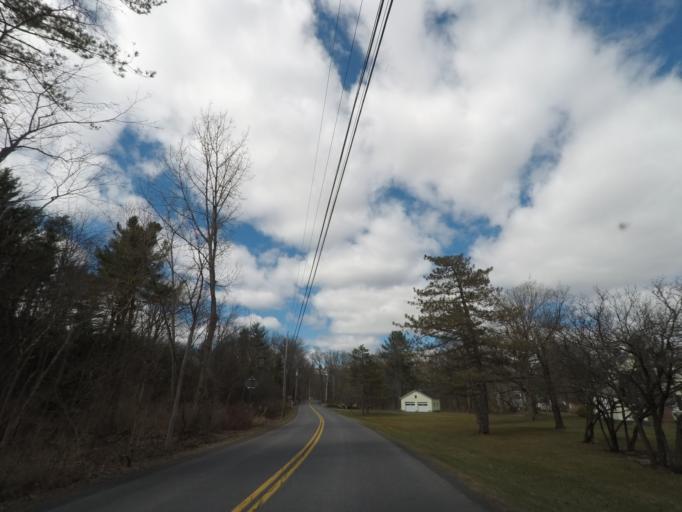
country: US
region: New York
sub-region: Albany County
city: Voorheesville
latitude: 42.6395
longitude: -73.9320
